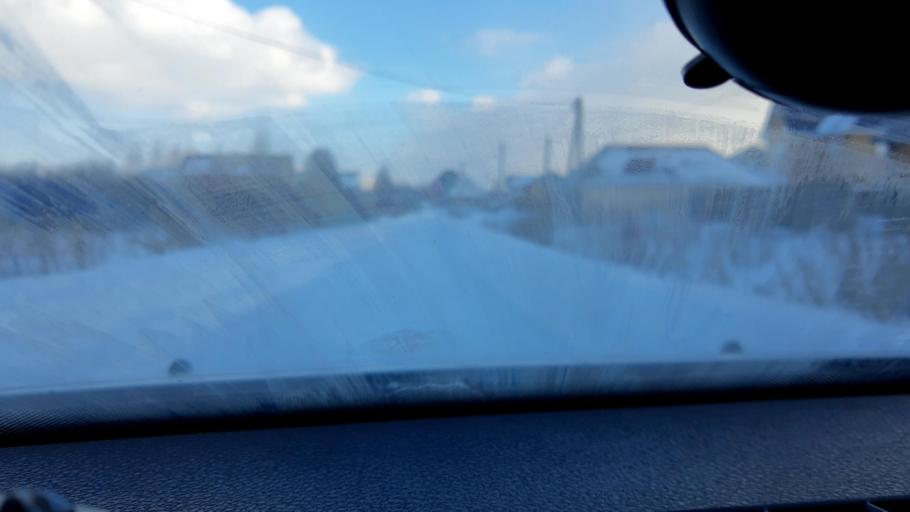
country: RU
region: Bashkortostan
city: Ufa
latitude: 54.6557
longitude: 56.0689
